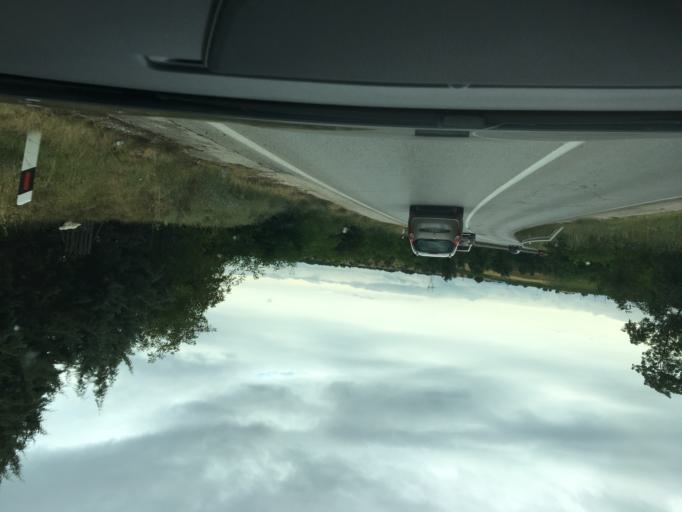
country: MK
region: Staro Nagoricane
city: Staro Nagorichane
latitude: 42.1753
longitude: 21.7902
